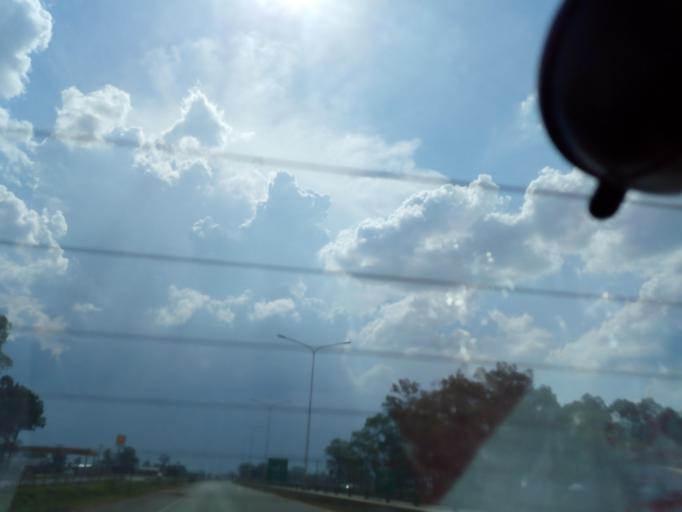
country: AR
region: Corrientes
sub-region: Departamento de Paso de los Libres
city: Paso de los Libres
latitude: -29.7220
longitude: -57.1448
